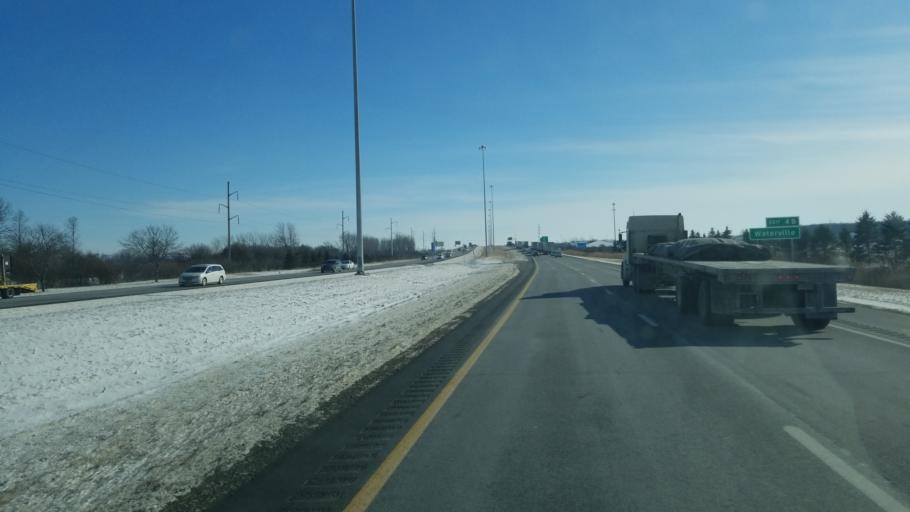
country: US
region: Ohio
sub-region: Lucas County
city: Maumee
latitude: 41.5666
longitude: -83.6907
